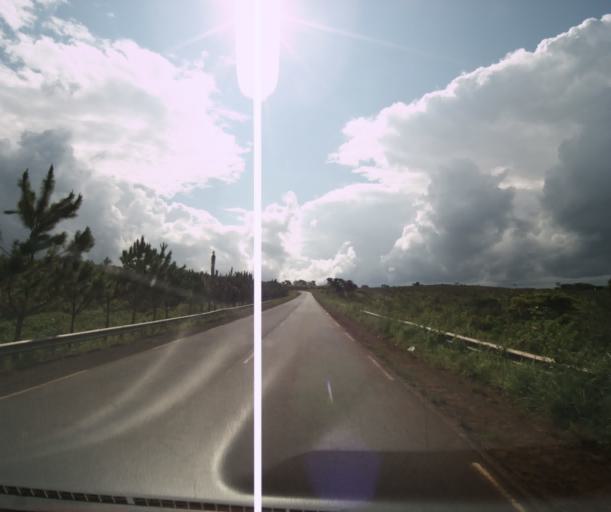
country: CM
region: West
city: Foumban
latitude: 5.7047
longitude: 10.8368
